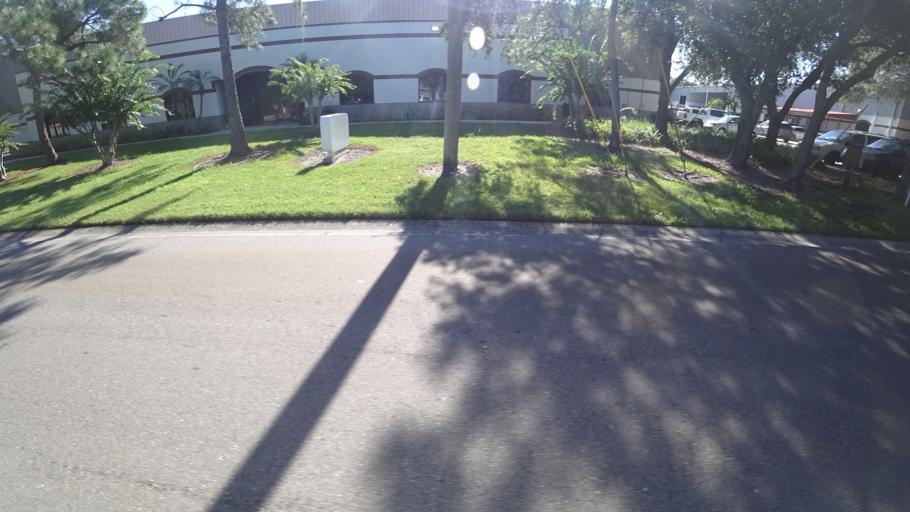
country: US
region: Florida
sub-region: Manatee County
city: Whitfield
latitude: 27.4279
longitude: -82.5362
